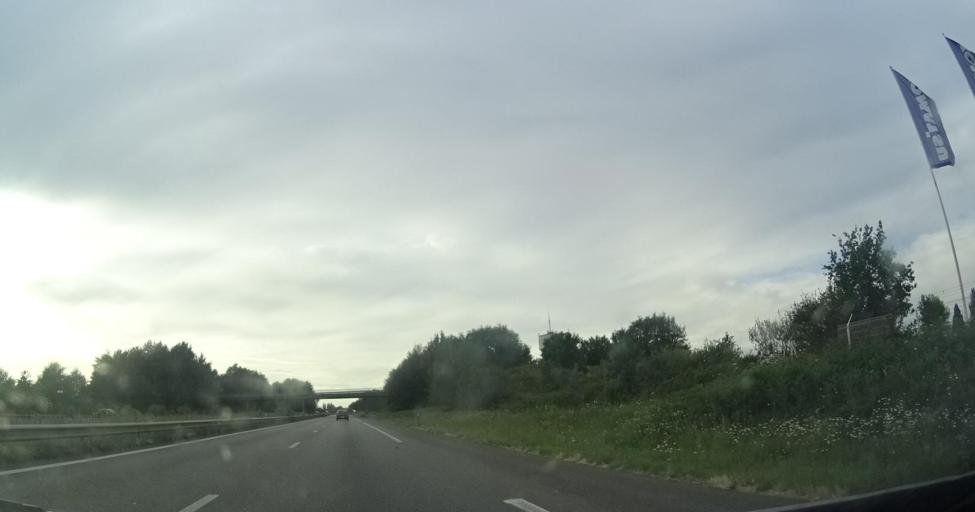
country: FR
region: Pays de la Loire
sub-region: Departement de la Loire-Atlantique
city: Vigneux-de-Bretagne
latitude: 47.2789
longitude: -1.7246
